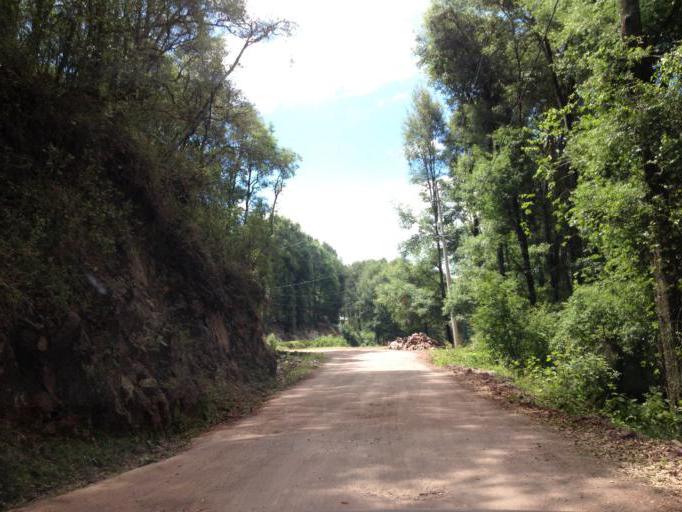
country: MX
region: Hidalgo
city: Mineral del Monte
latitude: 20.2041
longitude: -98.6606
